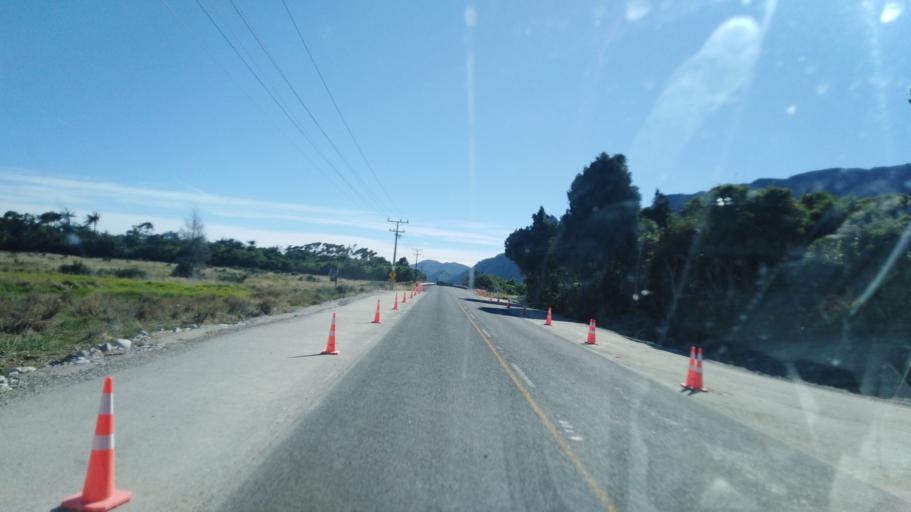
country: NZ
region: West Coast
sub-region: Buller District
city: Westport
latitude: -41.6679
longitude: 171.8085
